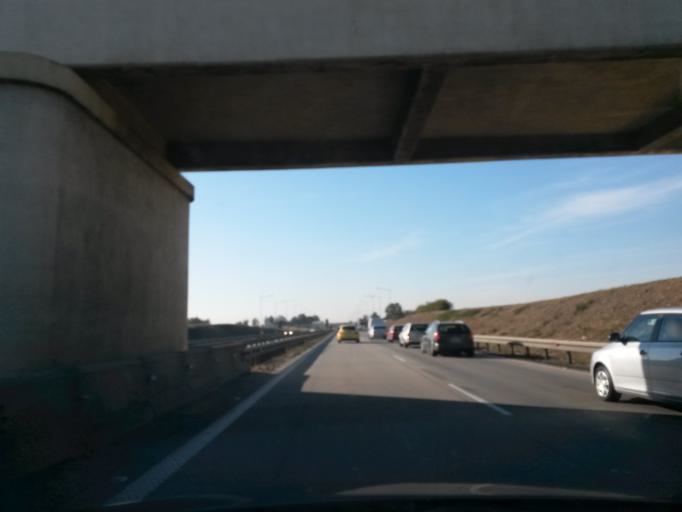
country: PL
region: Lower Silesian Voivodeship
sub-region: Powiat sredzki
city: Ciechow
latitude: 51.0408
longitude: 16.6023
